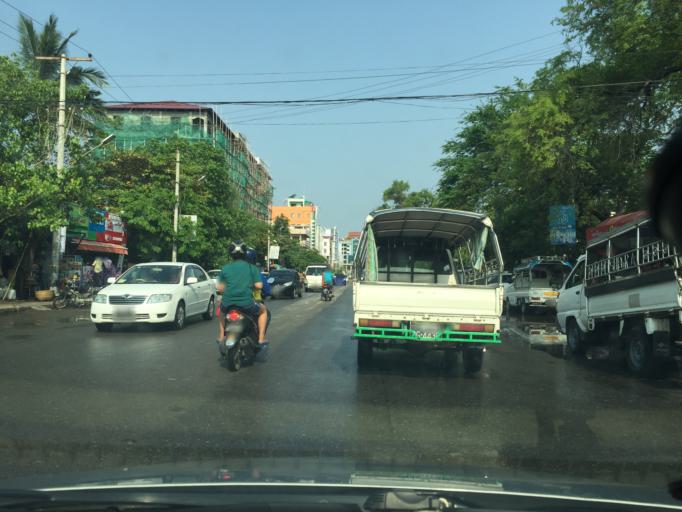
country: MM
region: Mandalay
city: Mandalay
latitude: 21.9766
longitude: 96.0919
